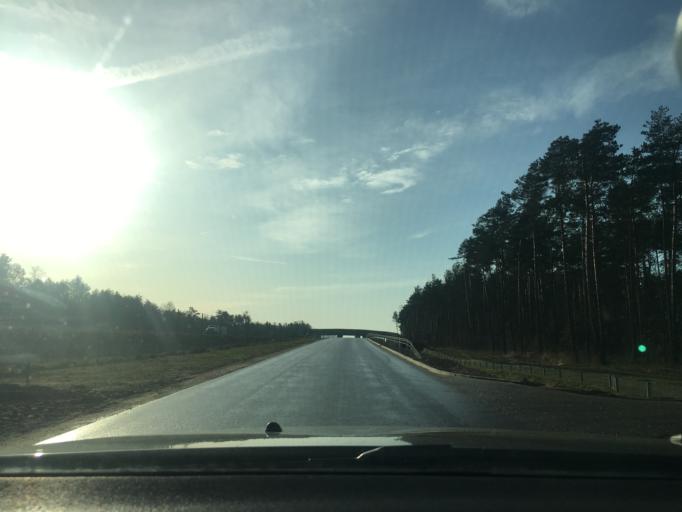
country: PL
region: Swietokrzyskie
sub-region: Powiat jedrzejowski
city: Jedrzejow
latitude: 50.6765
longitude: 20.3486
